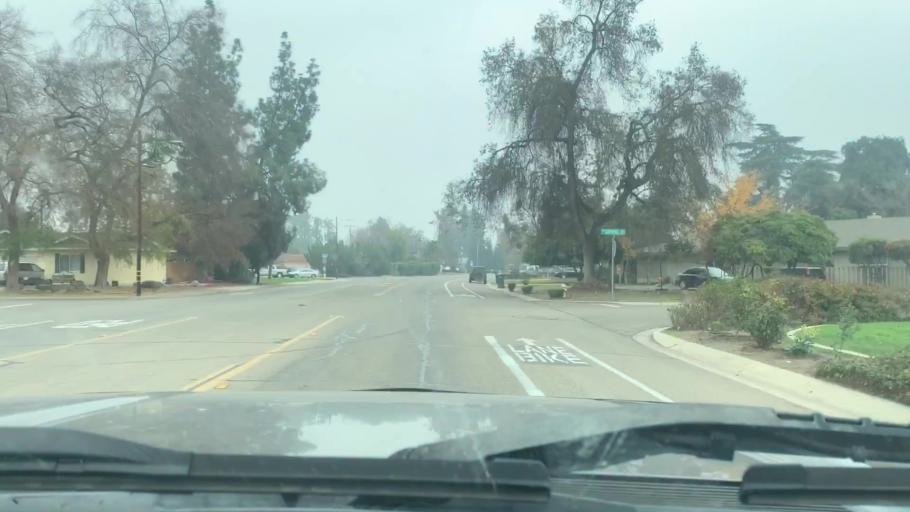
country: US
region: California
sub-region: Tulare County
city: Visalia
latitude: 36.3160
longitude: -119.3248
